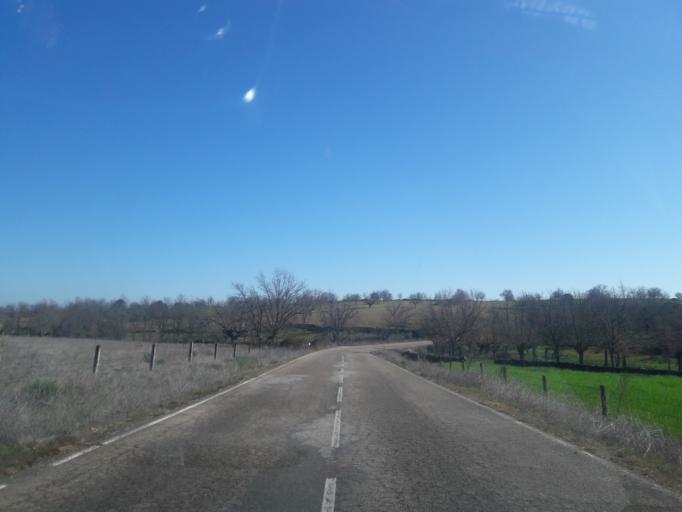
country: ES
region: Castille and Leon
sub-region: Provincia de Salamanca
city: Cabeza del Caballo
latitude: 41.1659
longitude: -6.5385
